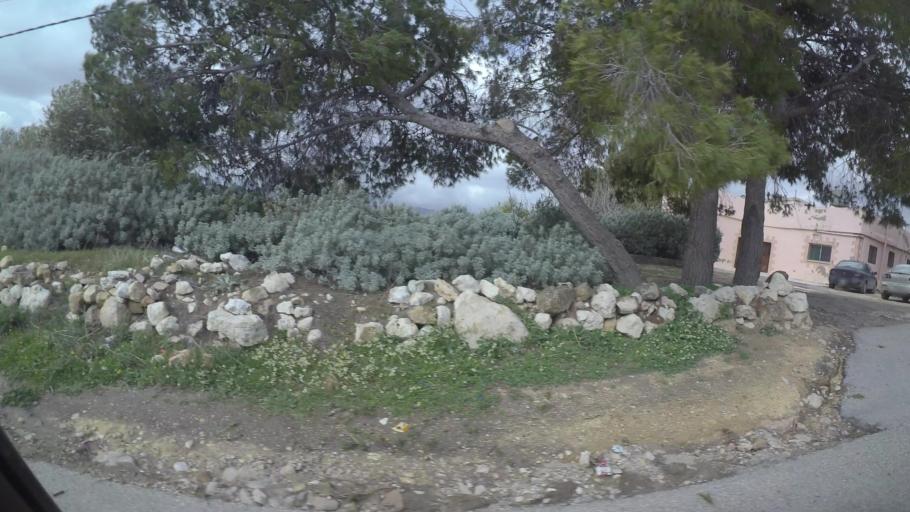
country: JO
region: Amman
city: Al Jubayhah
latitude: 32.0763
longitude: 35.8644
